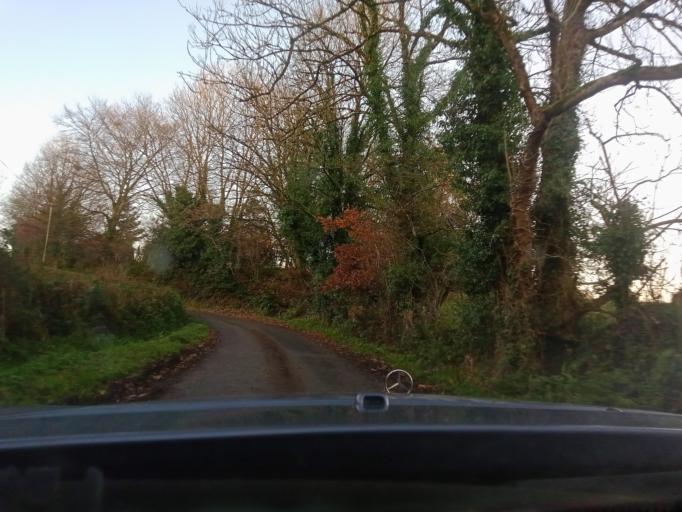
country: IE
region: Leinster
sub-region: Kilkenny
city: Graiguenamanagh
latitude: 52.4785
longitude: -6.9400
